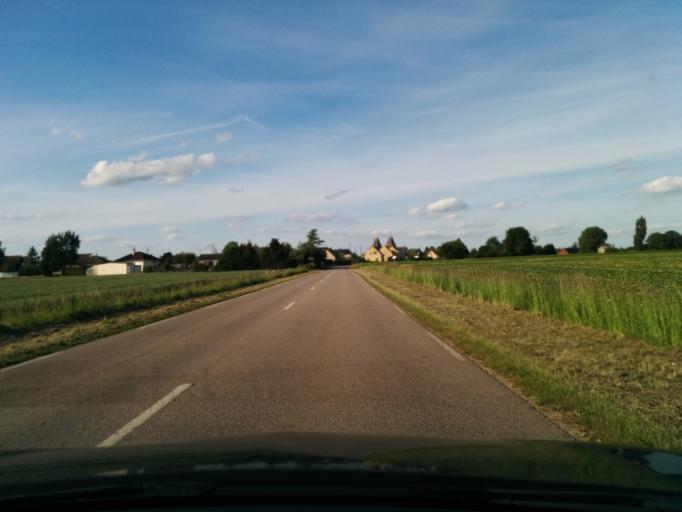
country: FR
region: Haute-Normandie
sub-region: Departement de l'Eure
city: Les Andelys
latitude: 49.3061
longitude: 1.4280
